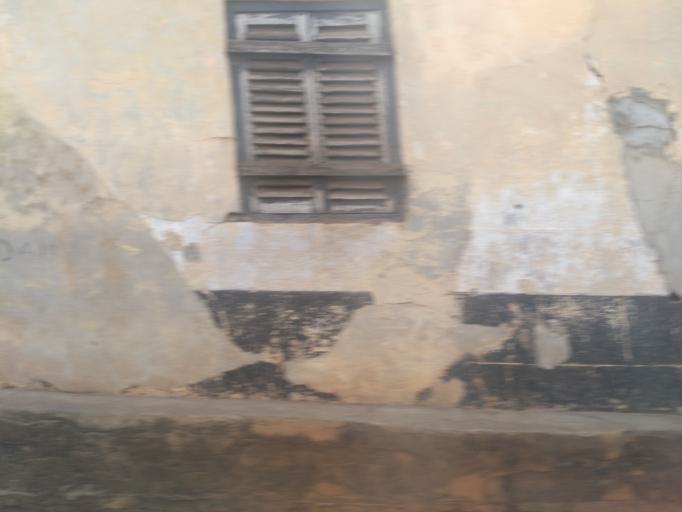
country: GH
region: Ashanti
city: Kumasi
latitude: 6.7041
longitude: -1.6194
